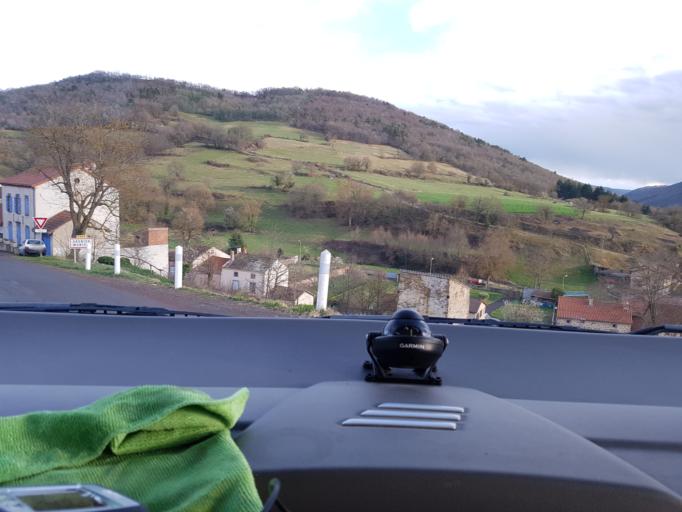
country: FR
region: Auvergne
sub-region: Departement du Cantal
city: Massiac
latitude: 45.2880
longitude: 3.1938
